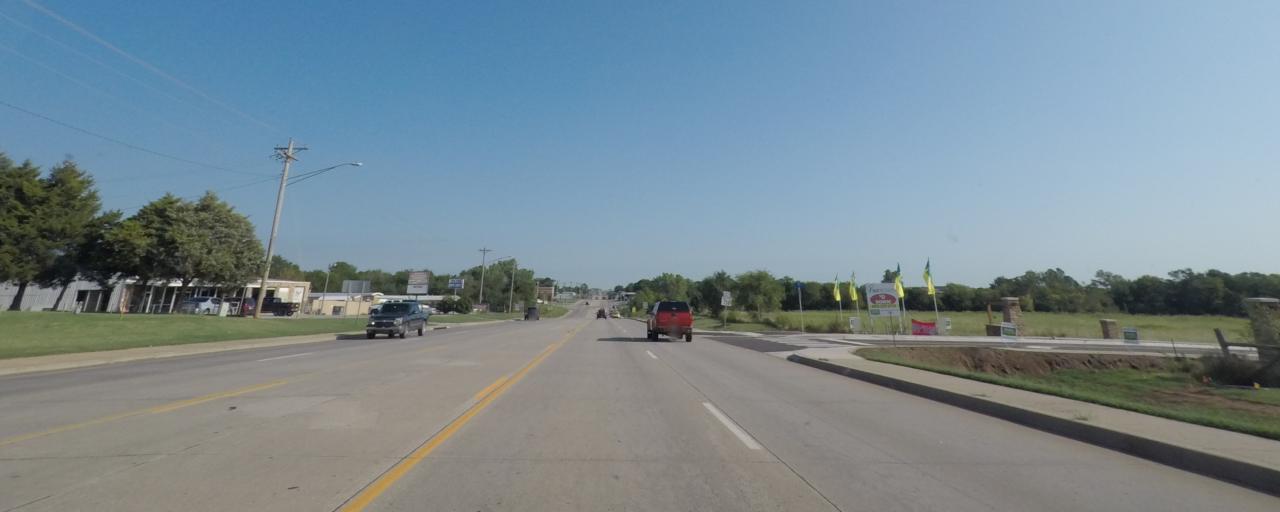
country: US
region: Oklahoma
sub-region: McClain County
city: Newcastle
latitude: 35.2442
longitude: -97.6002
